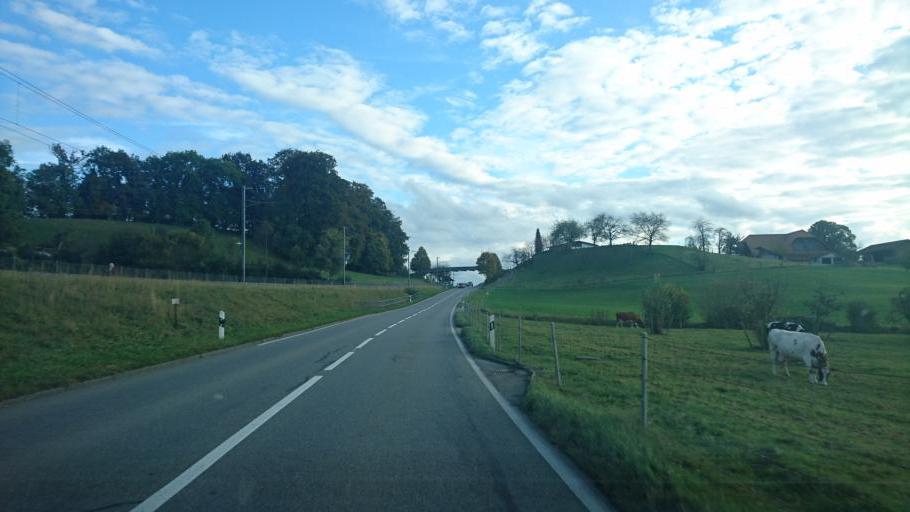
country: CH
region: Bern
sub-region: Bern-Mittelland District
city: Vechigen
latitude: 46.9487
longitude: 7.5555
